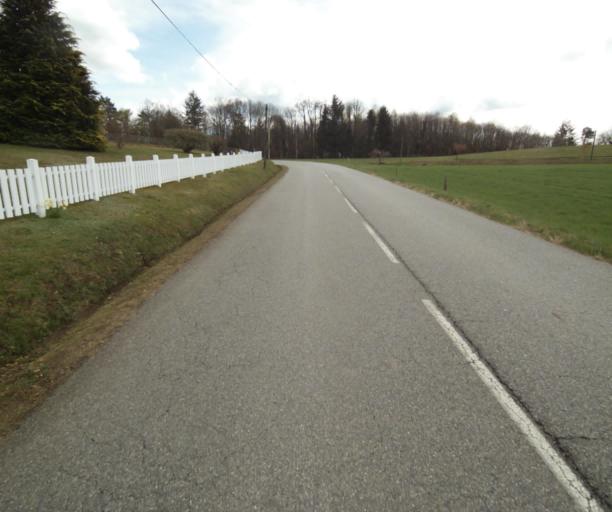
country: FR
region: Limousin
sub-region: Departement de la Correze
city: Laguenne
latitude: 45.2099
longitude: 1.8676
